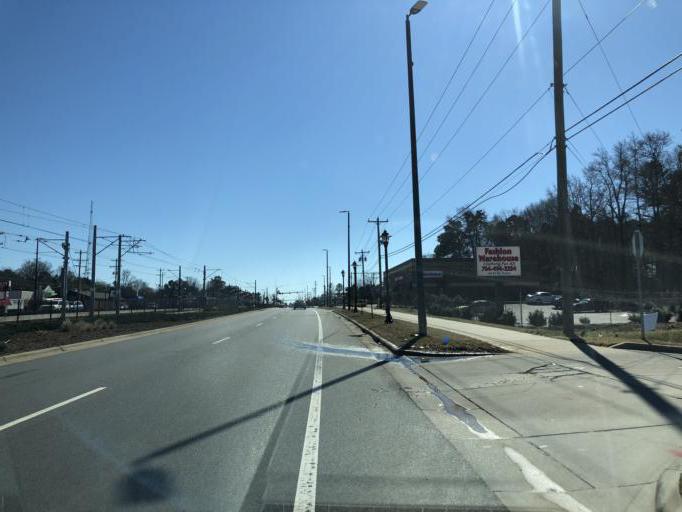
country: US
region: North Carolina
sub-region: Mecklenburg County
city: Charlotte
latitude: 35.2795
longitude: -80.7662
